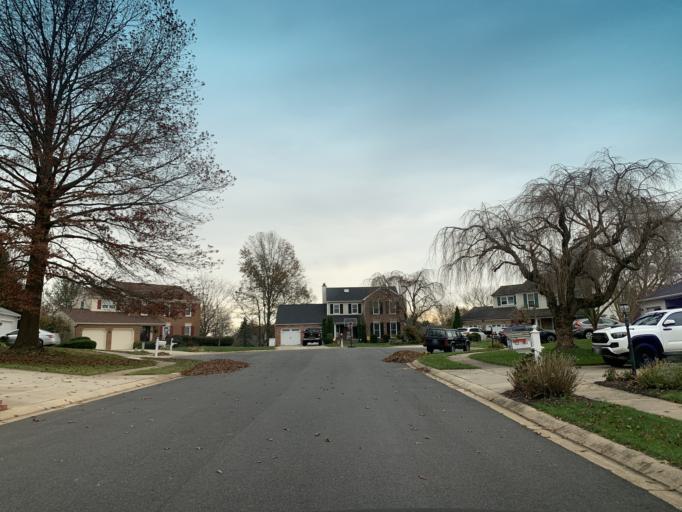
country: US
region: Maryland
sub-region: Harford County
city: Bel Air
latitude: 39.5453
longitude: -76.3409
